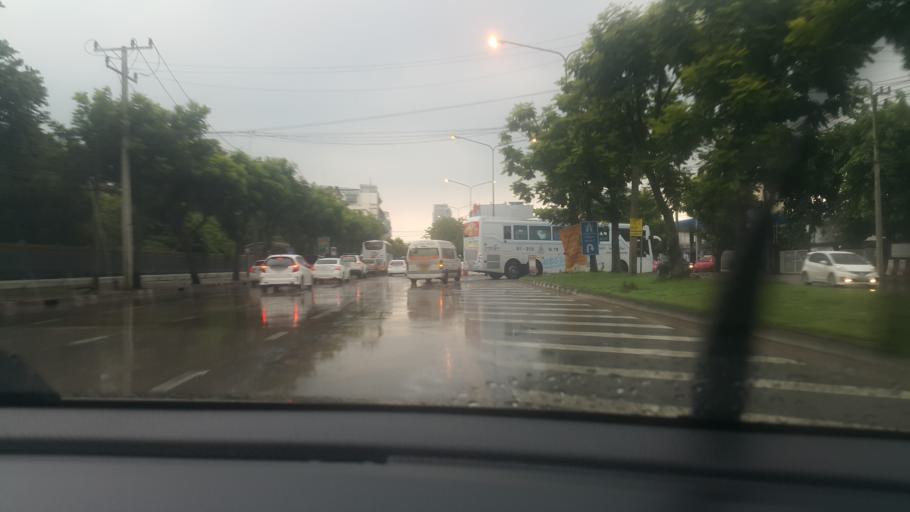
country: TH
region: Bangkok
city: Bang Sue
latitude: 13.8048
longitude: 100.5483
